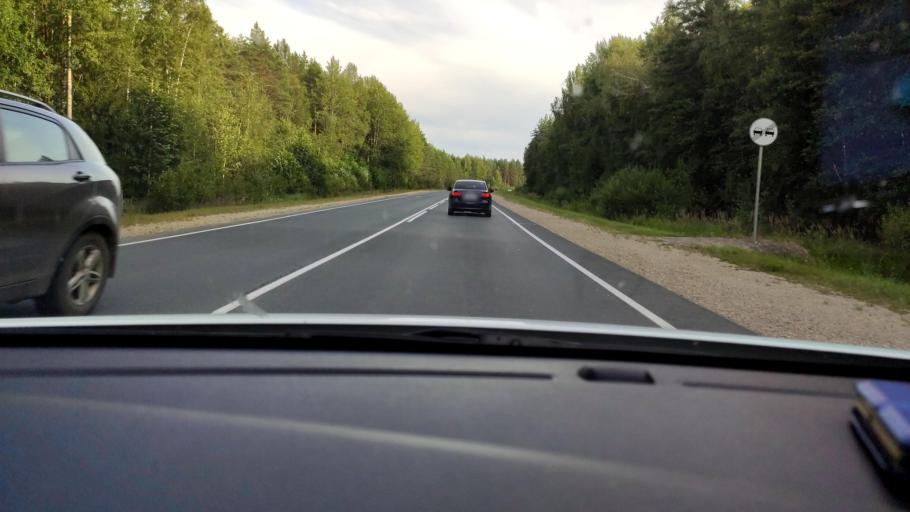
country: RU
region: Mariy-El
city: Suslonger
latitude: 56.3376
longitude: 48.2330
